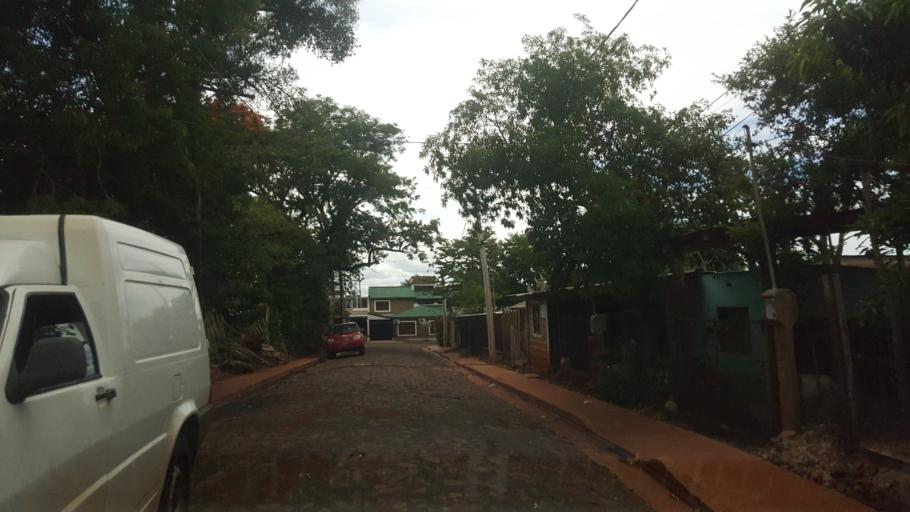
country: AR
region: Misiones
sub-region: Departamento de Capital
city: Posadas
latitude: -27.4013
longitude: -55.8958
